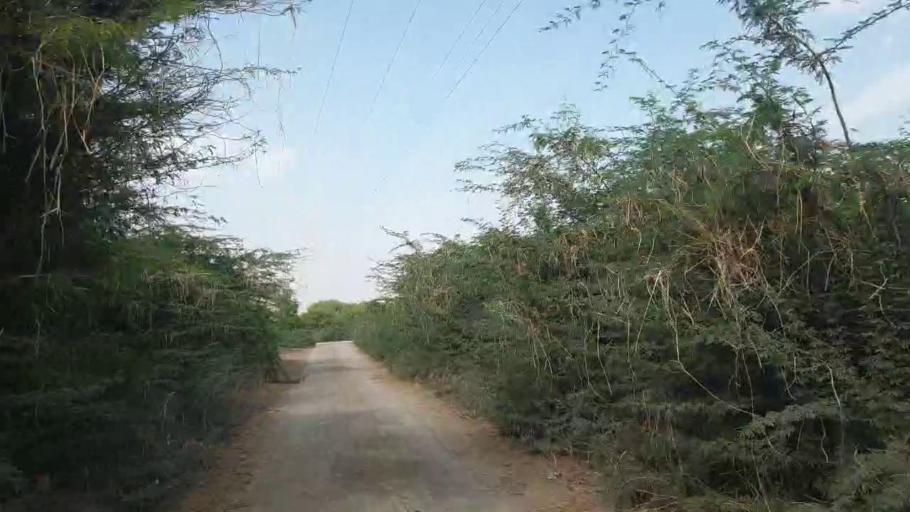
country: PK
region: Sindh
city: Digri
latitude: 25.0102
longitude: 69.0629
